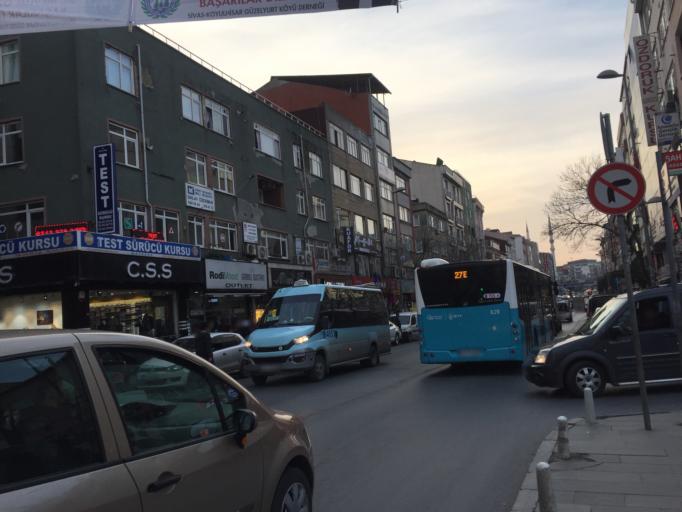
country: TR
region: Istanbul
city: Sisli
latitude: 41.0907
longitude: 29.0014
